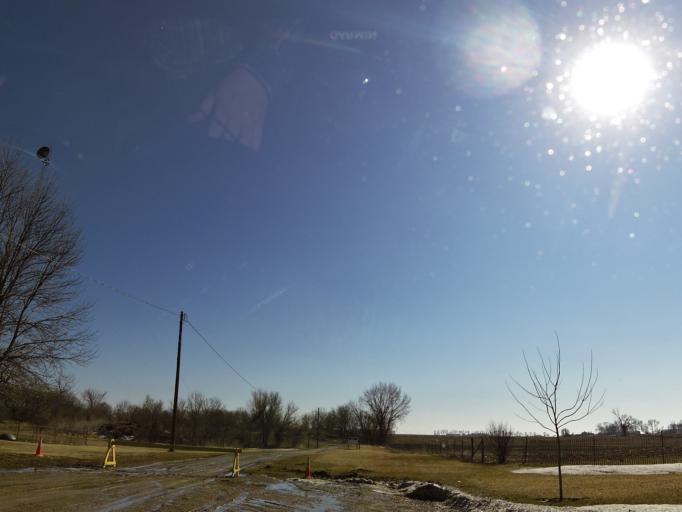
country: US
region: Minnesota
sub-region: Waseca County
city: New Richland
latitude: 43.8866
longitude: -93.4940
